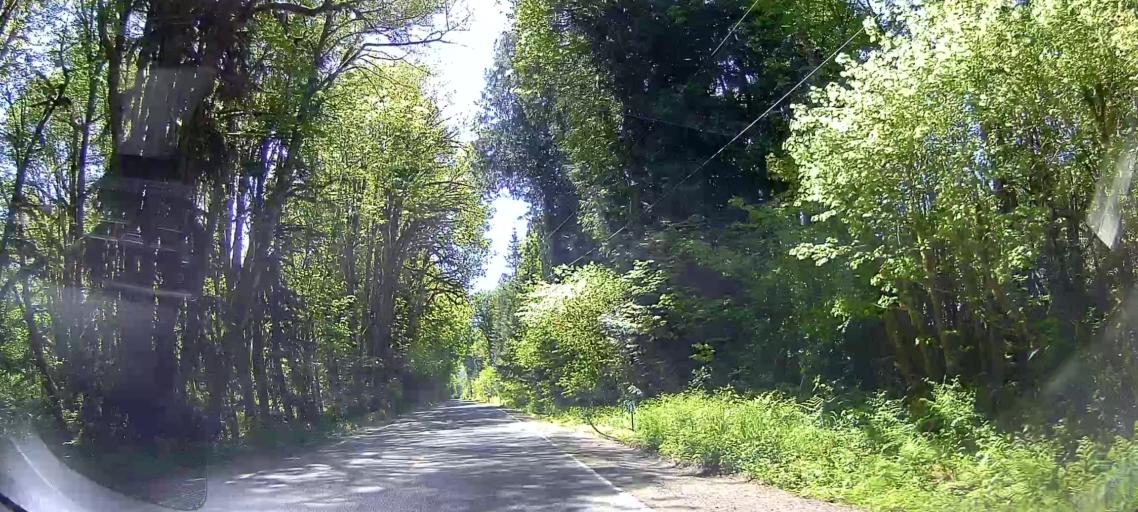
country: US
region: Washington
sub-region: Snohomish County
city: Darrington
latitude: 48.4966
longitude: -121.6599
